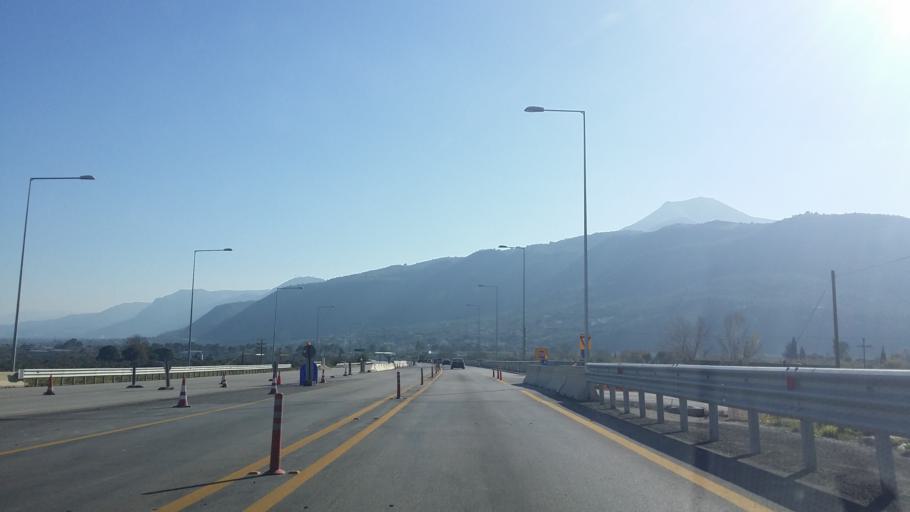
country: GR
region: West Greece
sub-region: Nomos Achaias
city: Aigio
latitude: 38.2350
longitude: 22.0793
